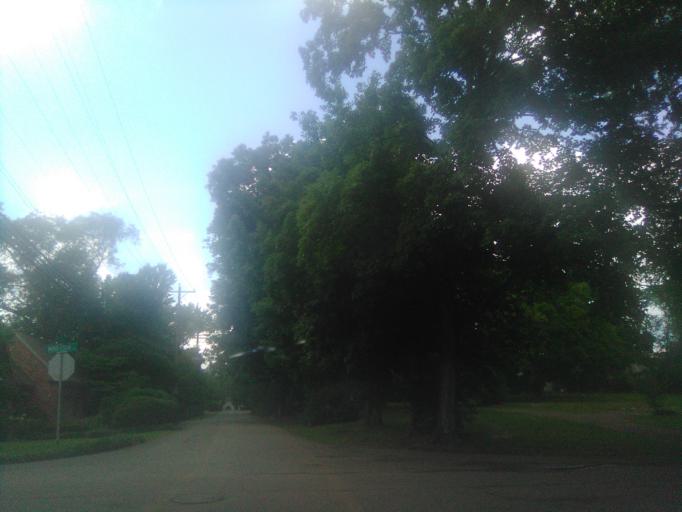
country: US
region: Tennessee
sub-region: Davidson County
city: Belle Meade
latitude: 36.1139
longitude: -86.8277
